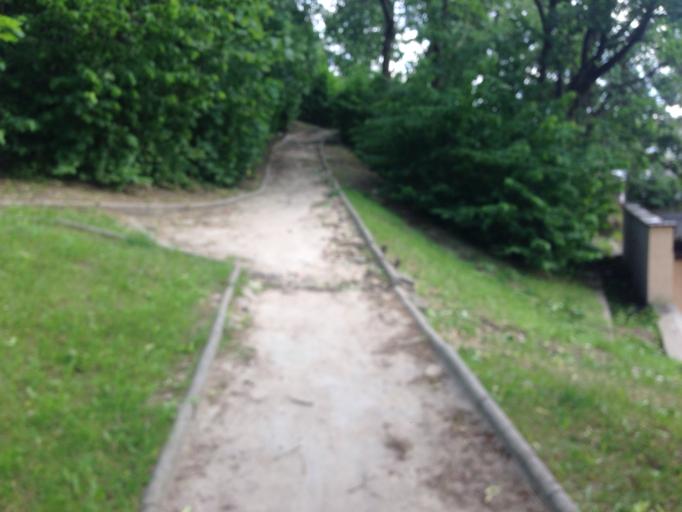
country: PL
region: Warmian-Masurian Voivodeship
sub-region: Powiat nidzicki
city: Nidzica
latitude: 53.3597
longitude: 20.4277
